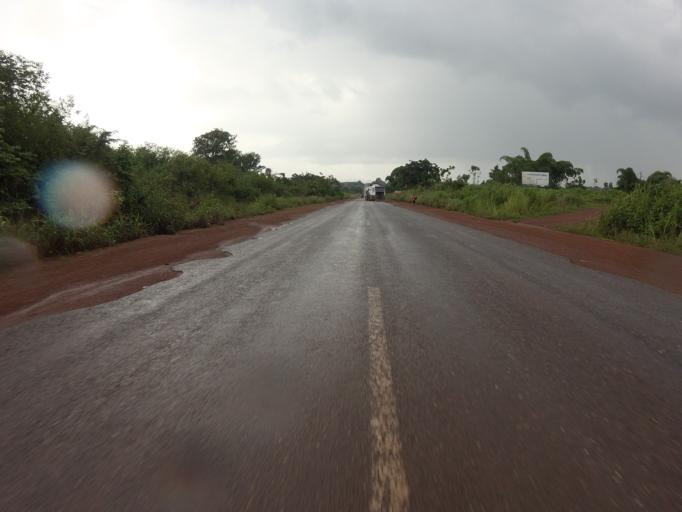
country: GH
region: Volta
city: Hohoe
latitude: 7.0319
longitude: 0.4273
